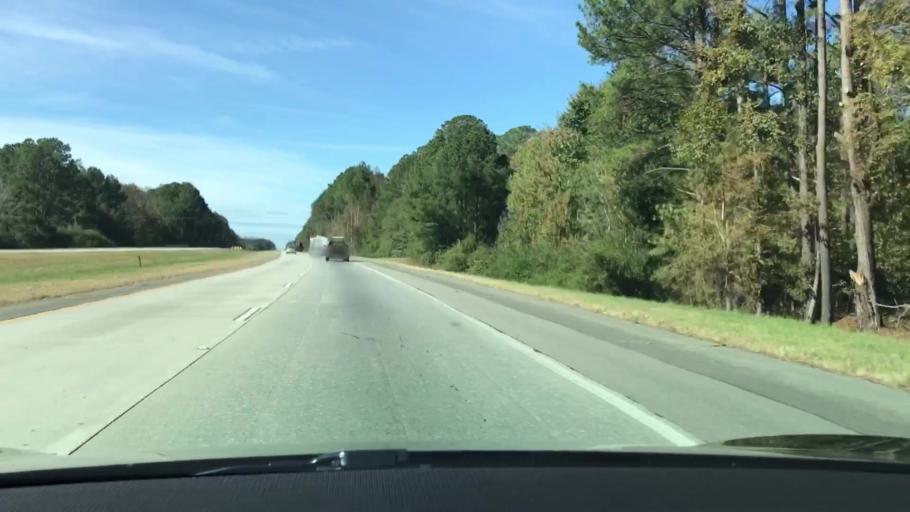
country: US
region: Georgia
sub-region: Greene County
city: Greensboro
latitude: 33.5498
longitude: -83.1331
